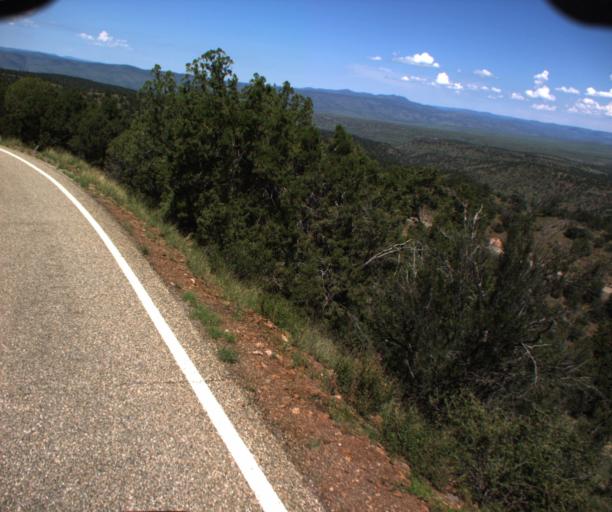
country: US
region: Arizona
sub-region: Greenlee County
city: Morenci
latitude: 33.2581
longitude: -109.3686
